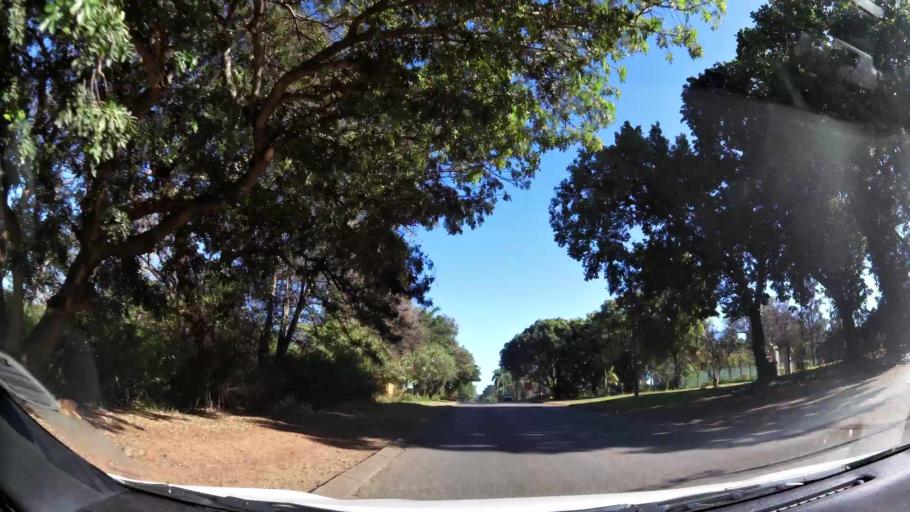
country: ZA
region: Limpopo
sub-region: Mopani District Municipality
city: Tzaneen
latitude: -23.8402
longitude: 30.1577
